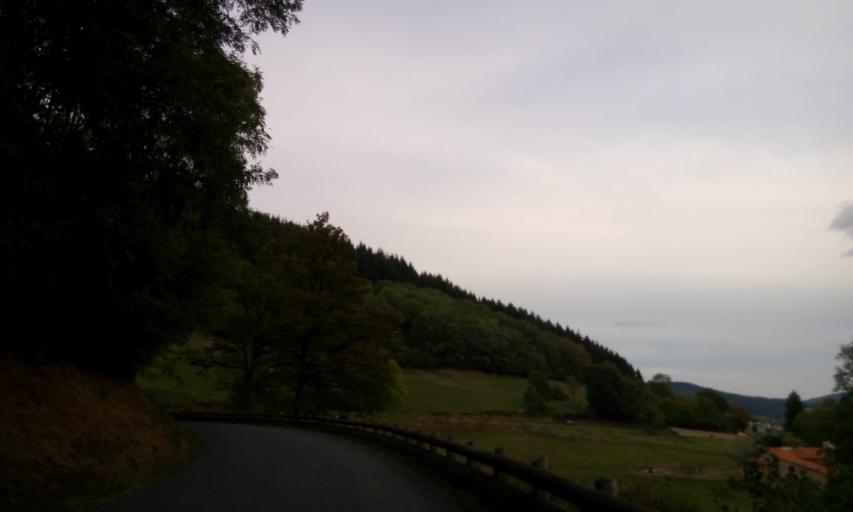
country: FR
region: Rhone-Alpes
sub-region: Departement du Rhone
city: Cublize
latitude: 46.0731
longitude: 4.3717
